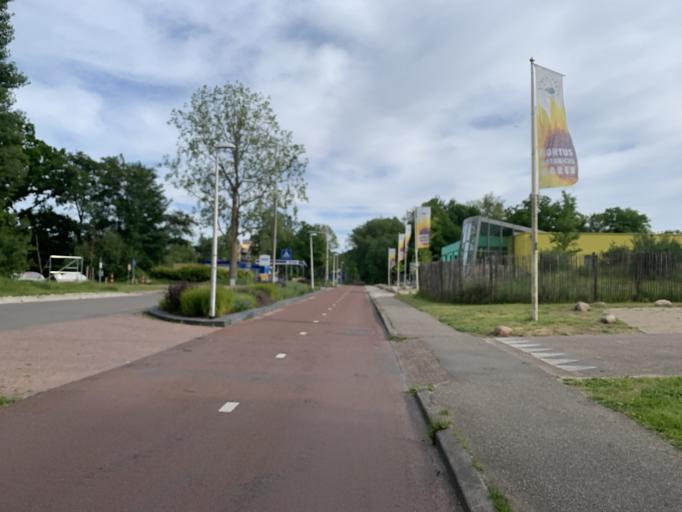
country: NL
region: Groningen
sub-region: Gemeente Haren
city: Haren
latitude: 53.1806
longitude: 6.6036
